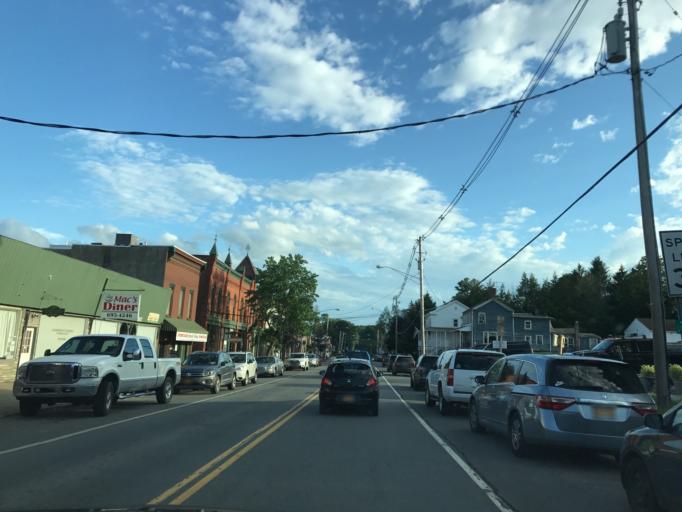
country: US
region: New York
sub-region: Saratoga County
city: Schuylerville
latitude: 43.0999
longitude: -73.5814
